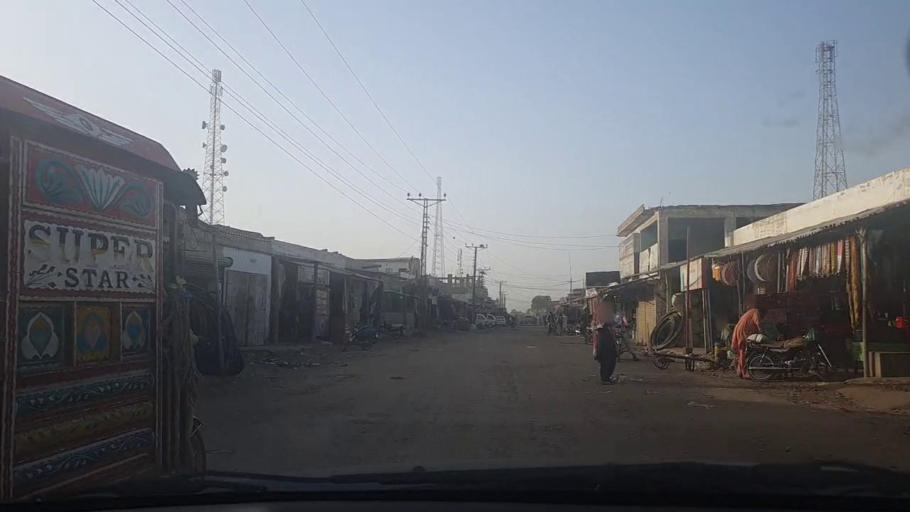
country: PK
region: Sindh
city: Keti Bandar
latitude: 24.3001
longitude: 67.6068
